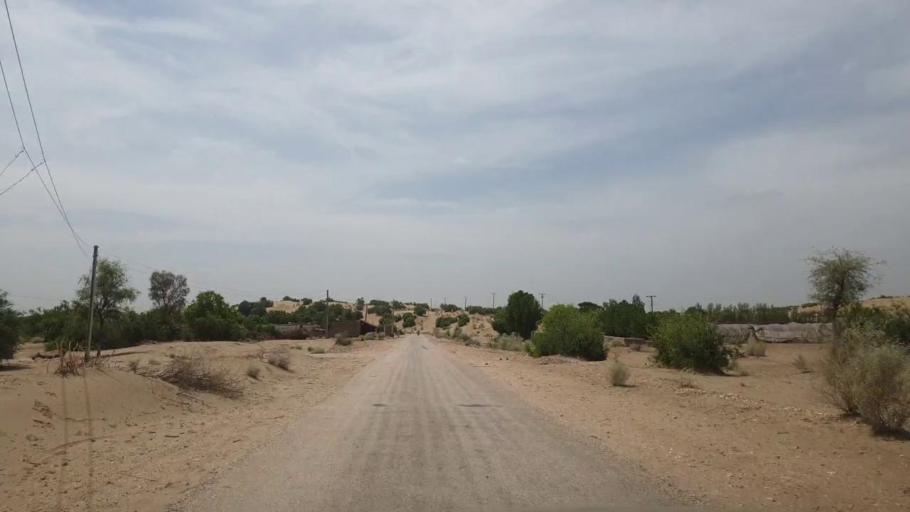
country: PK
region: Sindh
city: Kot Diji
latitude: 27.1079
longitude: 69.0769
